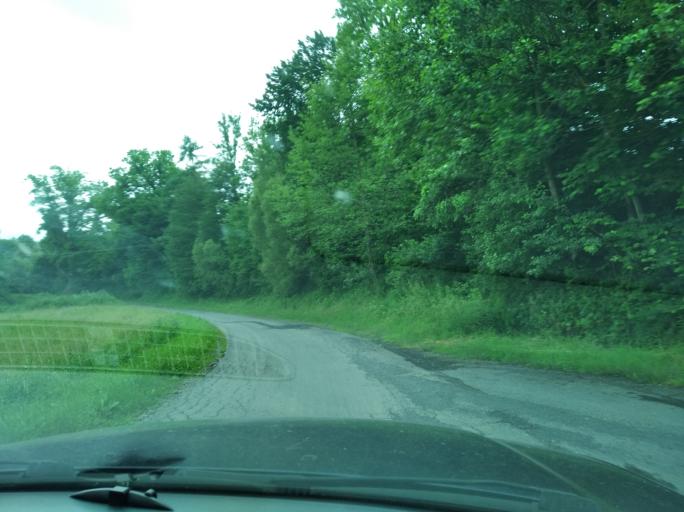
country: PL
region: Subcarpathian Voivodeship
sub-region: Powiat przemyski
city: Nienadowa
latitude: 49.8521
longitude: 22.4116
